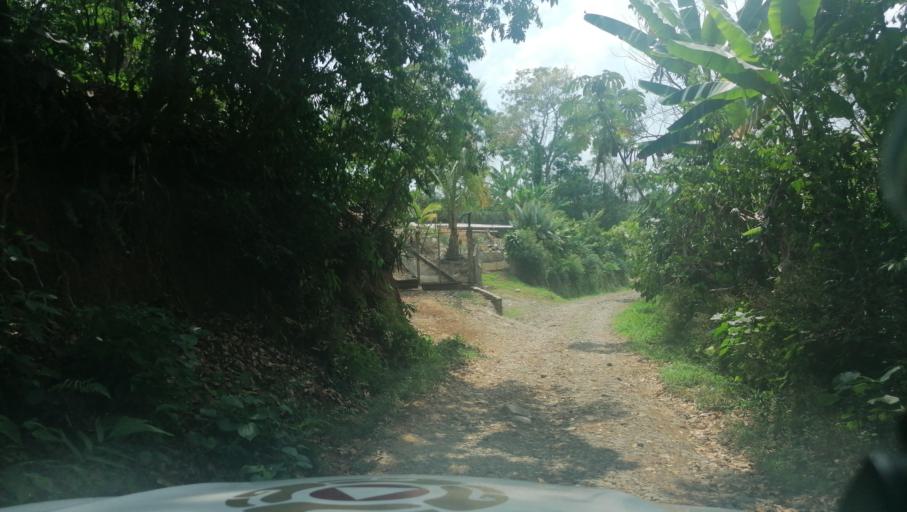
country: MX
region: Chiapas
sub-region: Cacahoatan
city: Benito Juarez
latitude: 15.0611
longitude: -92.2258
